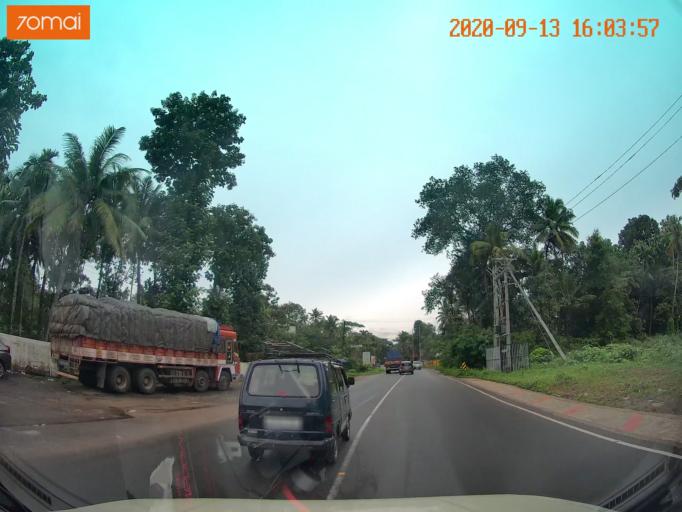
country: IN
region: Kerala
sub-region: Kottayam
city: Palackattumala
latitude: 9.6730
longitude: 76.5670
